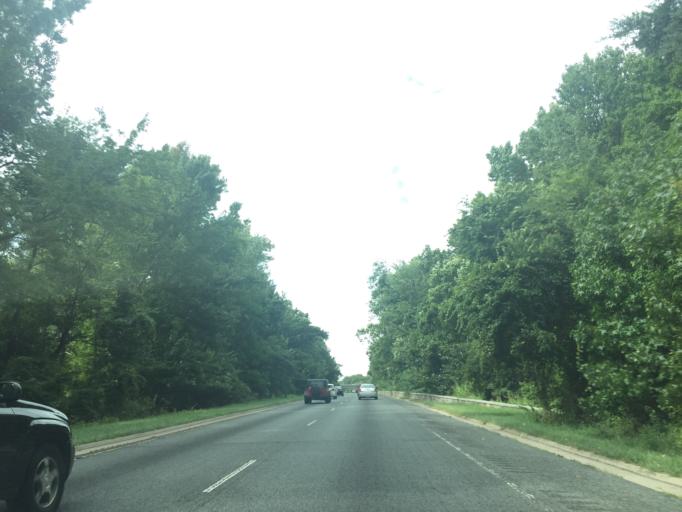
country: US
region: Maryland
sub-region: Anne Arundel County
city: Maryland City
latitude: 39.1004
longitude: -76.7978
